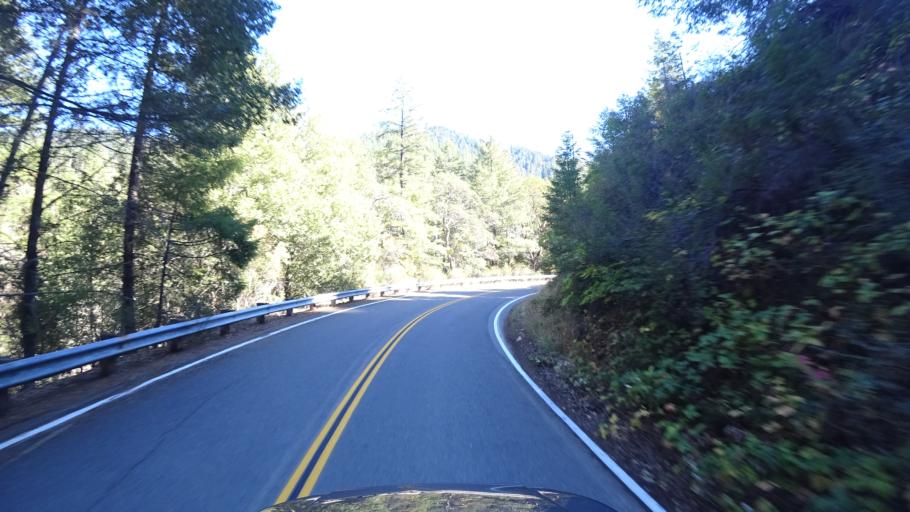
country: US
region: California
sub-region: Siskiyou County
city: Happy Camp
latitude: 41.3611
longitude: -123.4135
